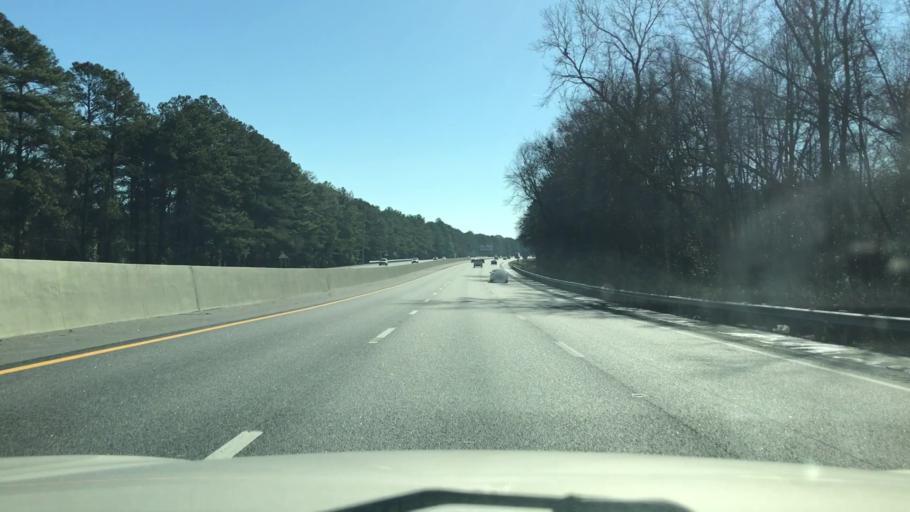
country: US
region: South Carolina
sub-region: Lexington County
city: Pineridge
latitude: 33.9138
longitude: -81.0591
